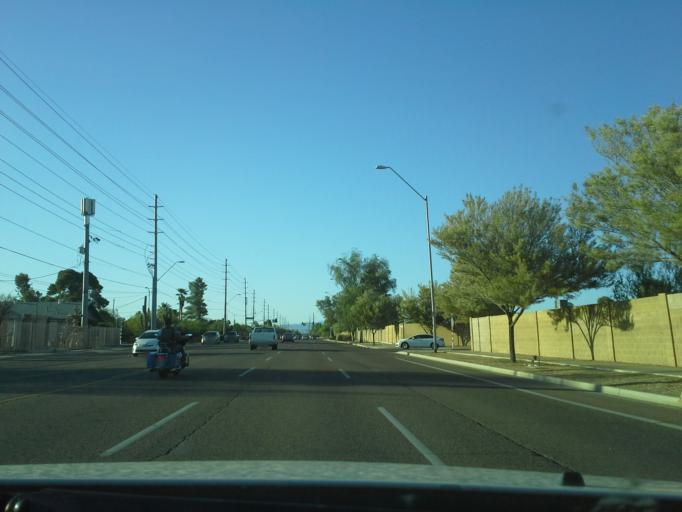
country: US
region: Arizona
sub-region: Maricopa County
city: Paradise Valley
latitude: 33.6457
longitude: -112.0134
